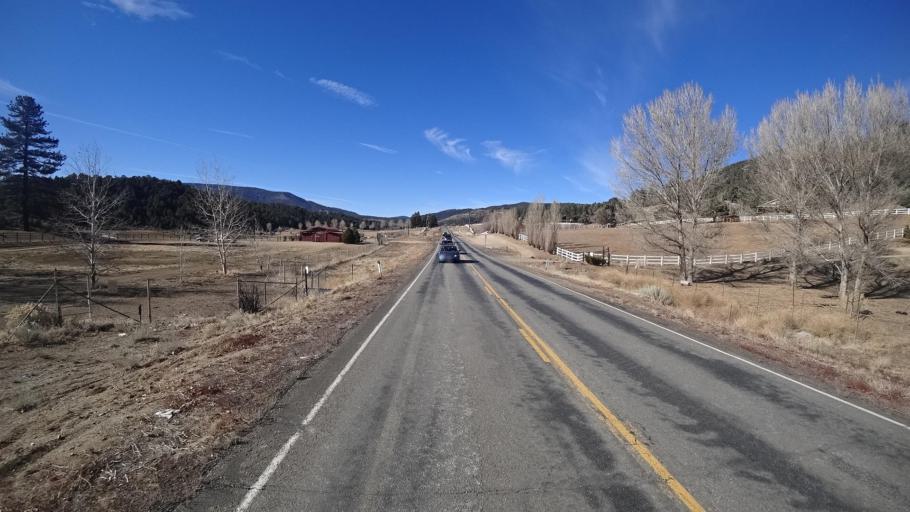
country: US
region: California
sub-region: Kern County
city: Frazier Park
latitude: 34.8288
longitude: -119.0232
